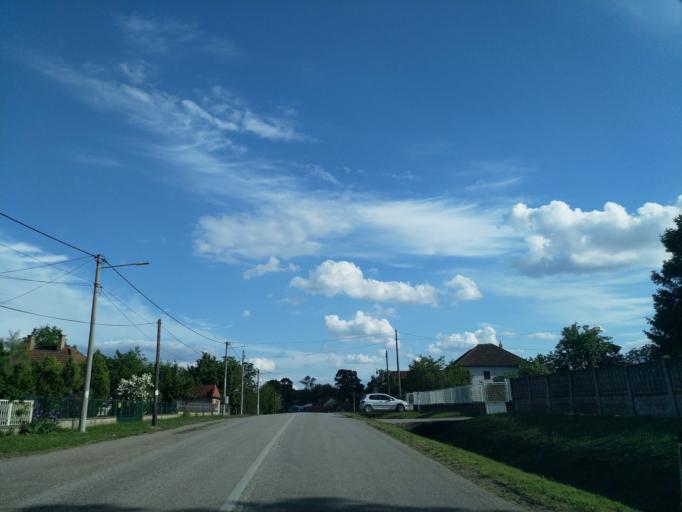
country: RS
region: Central Serbia
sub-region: Sumadijski Okrug
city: Lapovo
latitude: 44.1716
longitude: 21.0915
